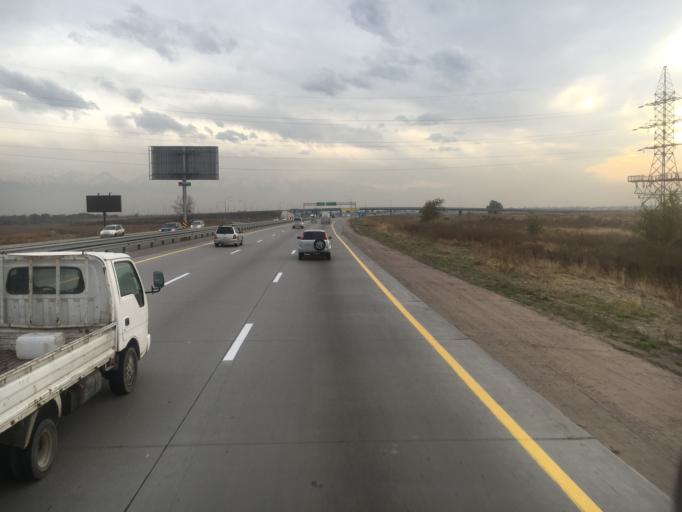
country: KZ
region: Almaty Oblysy
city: Pervomayskiy
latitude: 43.3954
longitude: 76.9746
